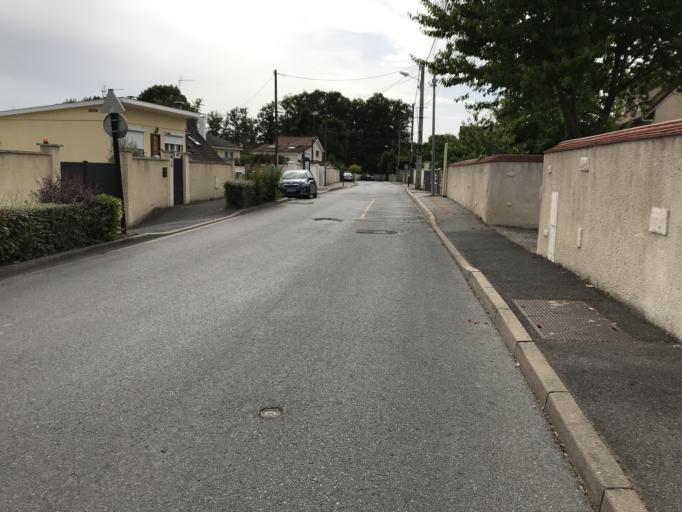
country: FR
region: Ile-de-France
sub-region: Departement de l'Essonne
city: La Ville-du-Bois
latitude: 48.6648
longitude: 2.2606
